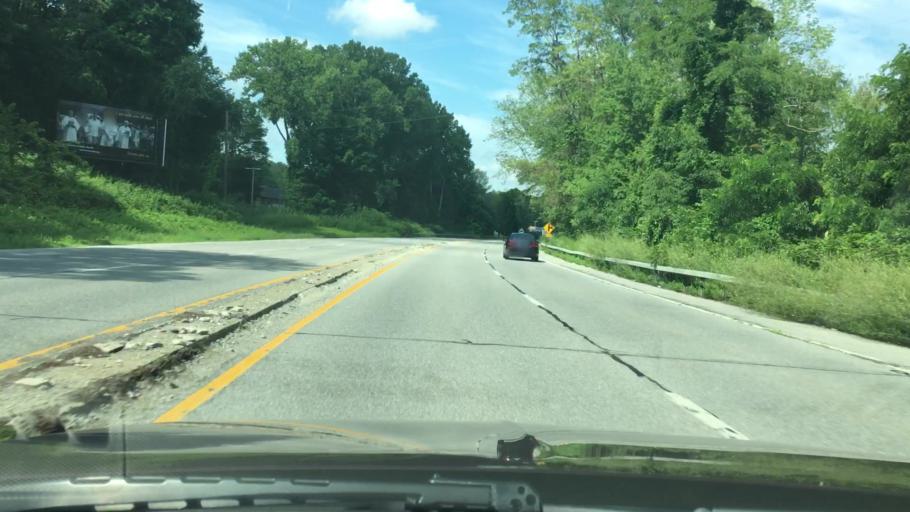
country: US
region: New York
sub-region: Putnam County
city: Peach Lake
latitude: 41.3875
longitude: -73.5528
